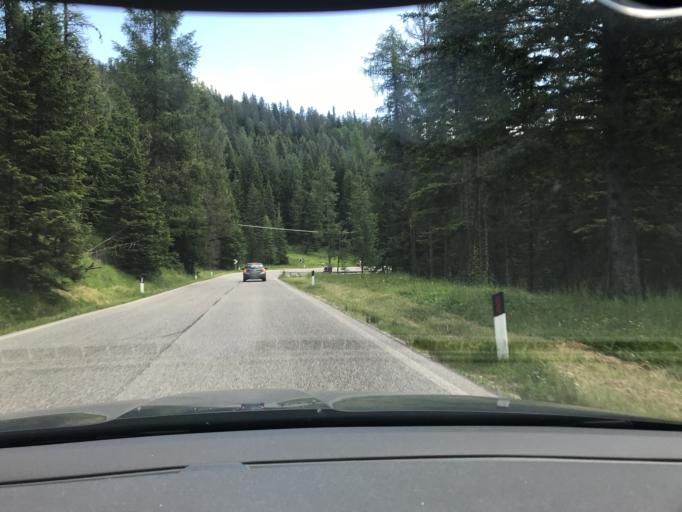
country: IT
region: Veneto
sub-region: Provincia di Belluno
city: Cortina d'Ampezzo
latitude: 46.5215
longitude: 12.0811
